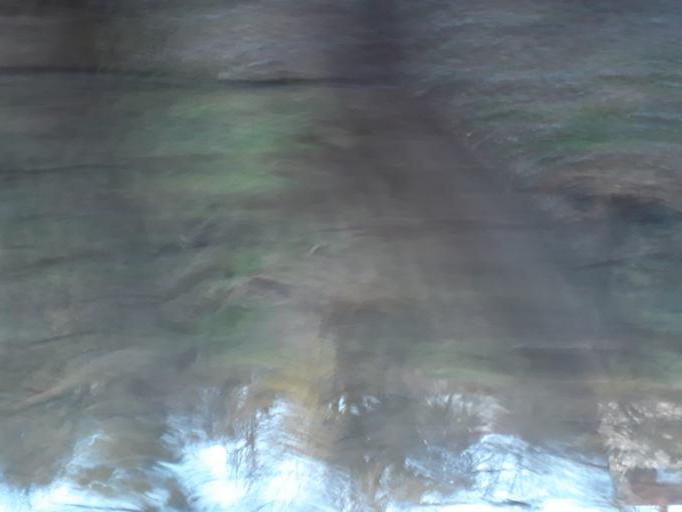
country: DE
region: Saxony
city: Reinhardtsgrimma
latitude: 50.9084
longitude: 13.7879
